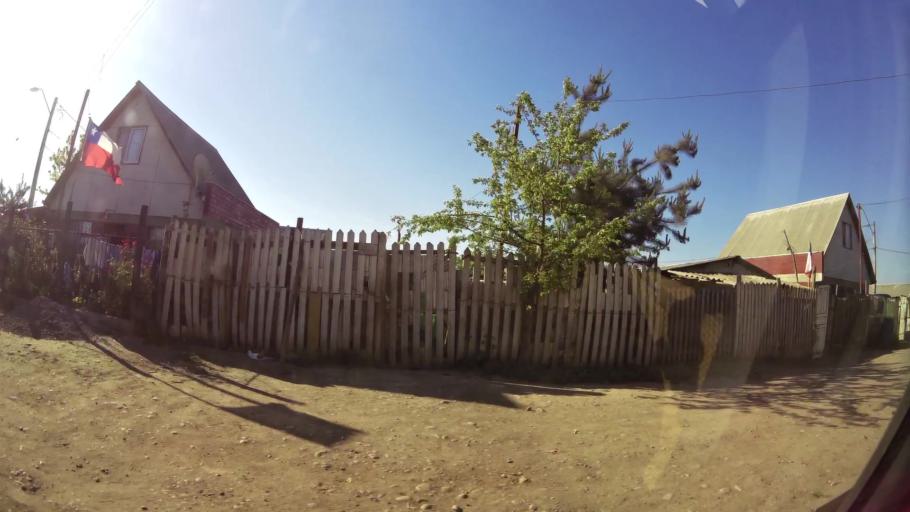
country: CL
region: Santiago Metropolitan
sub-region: Provincia de Talagante
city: Penaflor
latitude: -33.6161
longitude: -70.8726
